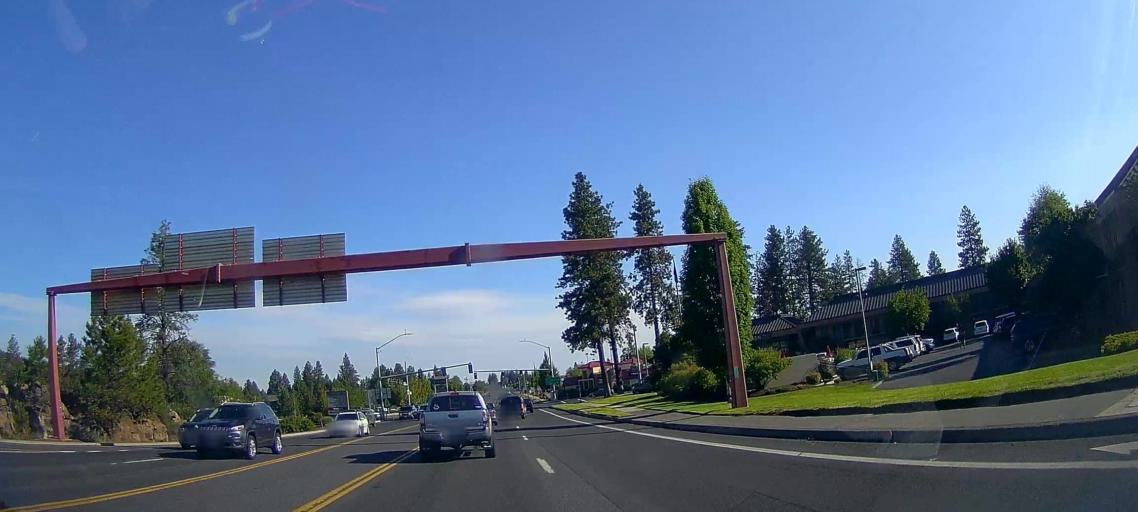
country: US
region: Oregon
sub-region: Deschutes County
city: Bend
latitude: 44.0784
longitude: -121.3047
